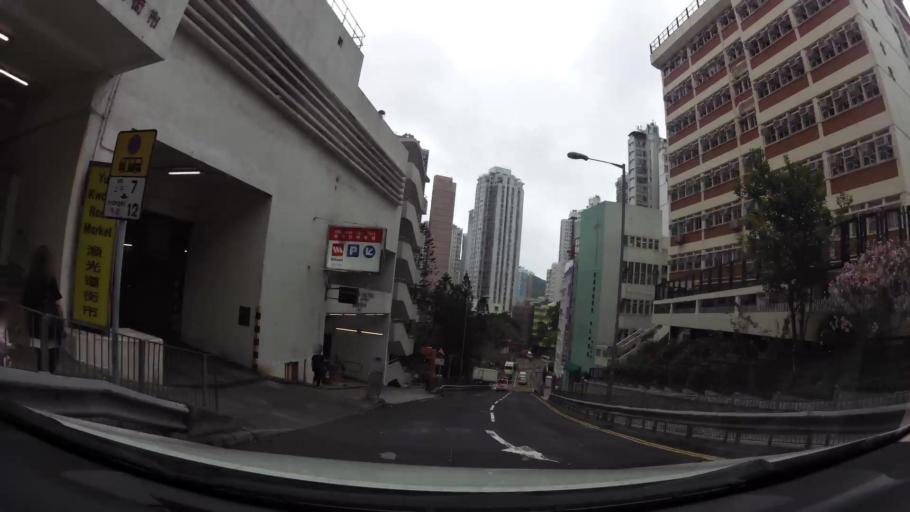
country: HK
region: Central and Western
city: Central
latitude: 22.2506
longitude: 114.1565
